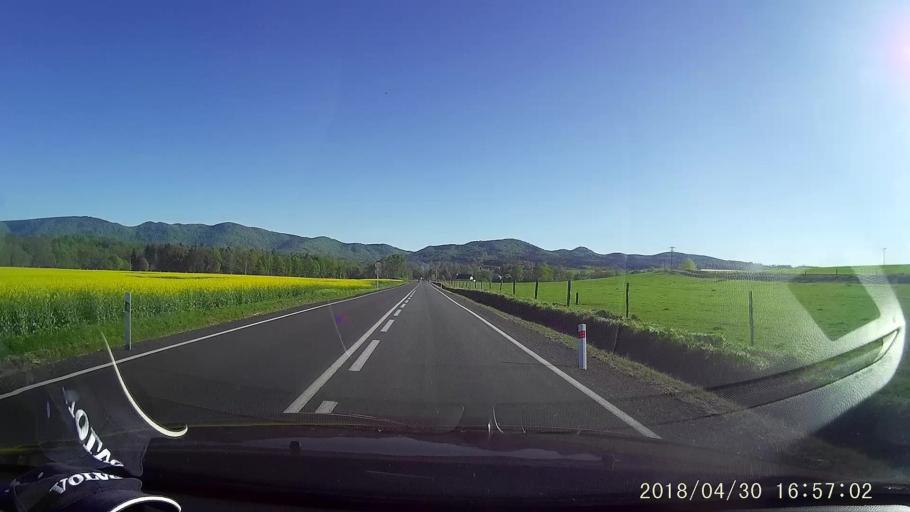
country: CZ
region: Liberecky
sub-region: Okres Liberec
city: Raspenava
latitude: 50.9127
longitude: 15.1199
